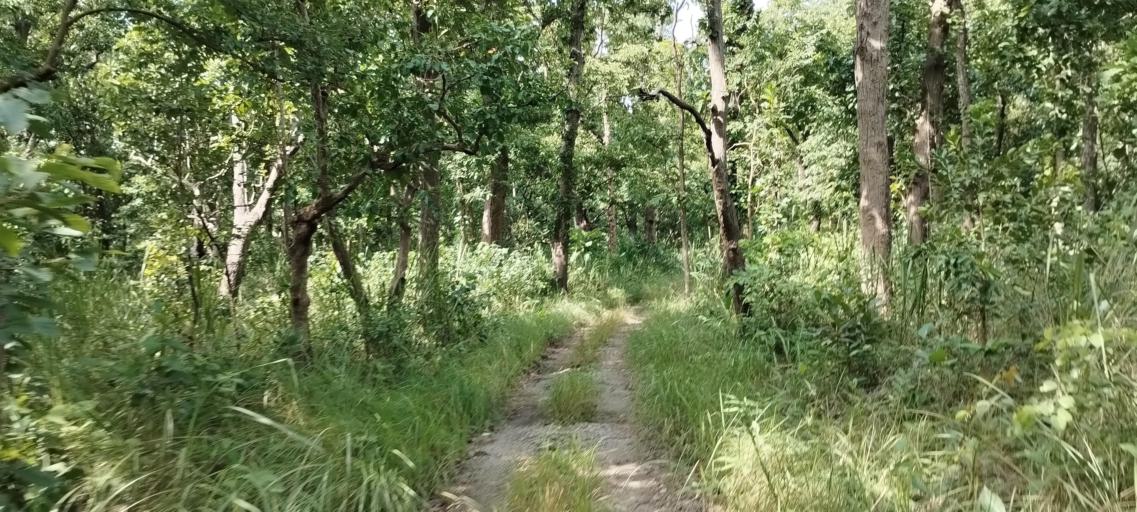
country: NP
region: Far Western
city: Tikapur
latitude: 28.5560
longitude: 81.2924
